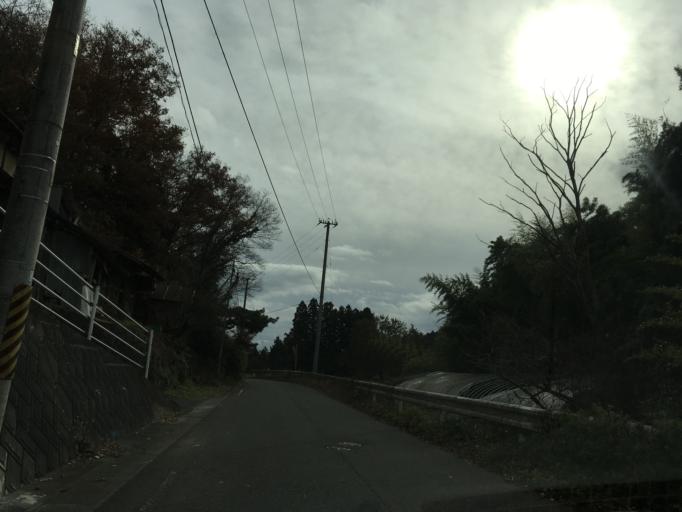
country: JP
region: Iwate
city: Ichinoseki
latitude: 38.7712
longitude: 141.2688
